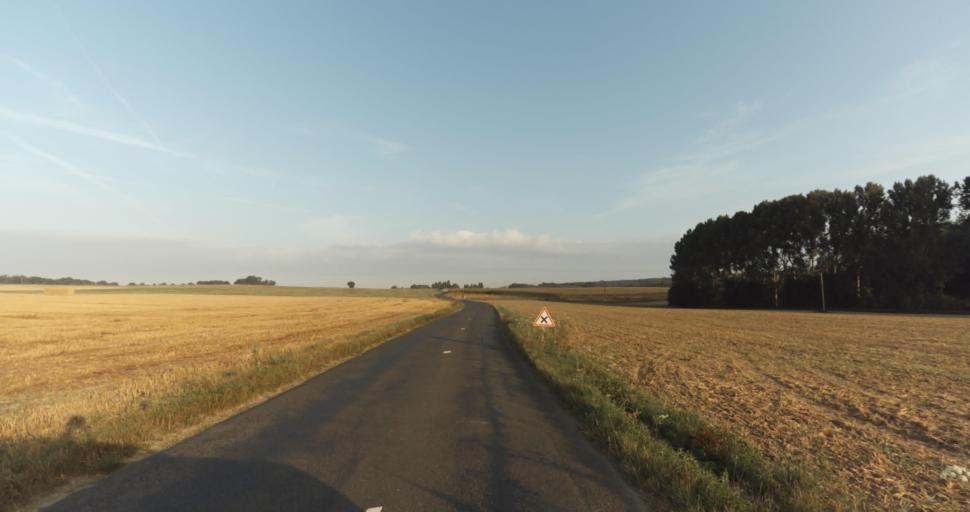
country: FR
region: Haute-Normandie
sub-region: Departement de l'Eure
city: Marcilly-sur-Eure
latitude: 48.7904
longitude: 1.3327
